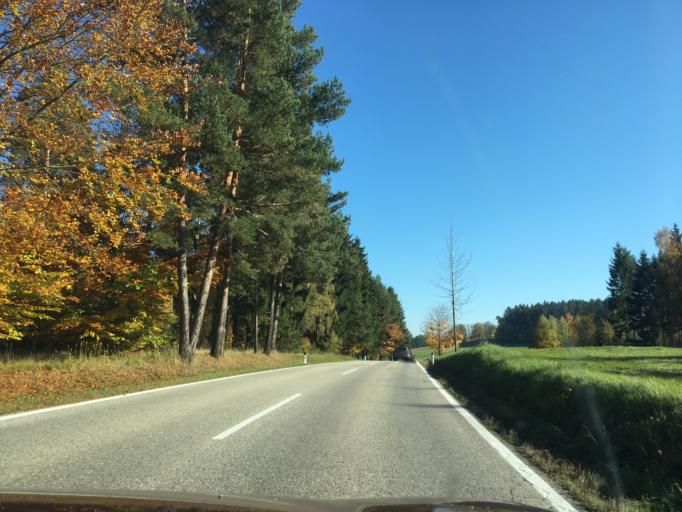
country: AT
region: Upper Austria
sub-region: Politischer Bezirk Freistadt
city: Freistadt
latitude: 48.5090
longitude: 14.5268
